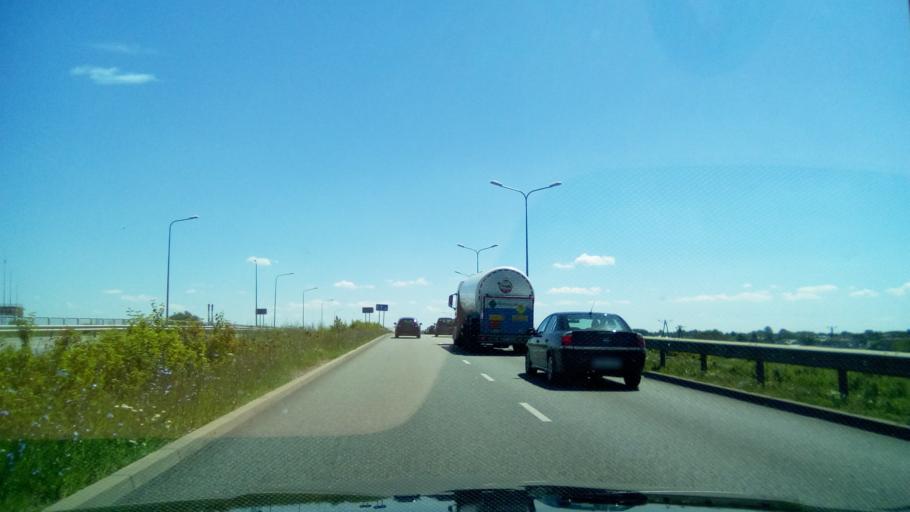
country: PL
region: Masovian Voivodeship
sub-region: Radom
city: Radom
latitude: 51.4201
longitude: 21.1838
